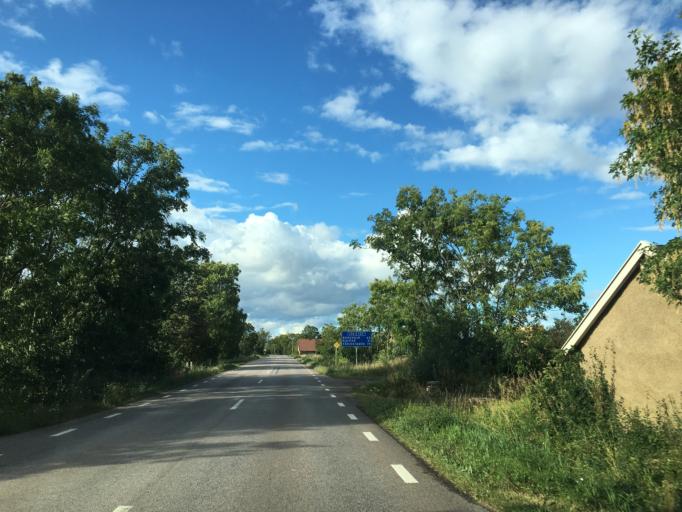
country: SE
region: Kalmar
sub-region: Morbylanga Kommun
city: Moerbylanga
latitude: 56.5199
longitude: 16.4400
